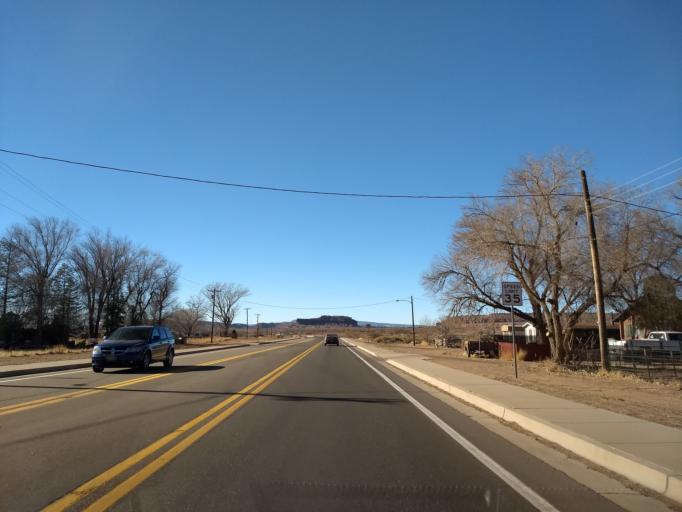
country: US
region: Arizona
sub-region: Coconino County
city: Fredonia
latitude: 36.9460
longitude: -112.5313
